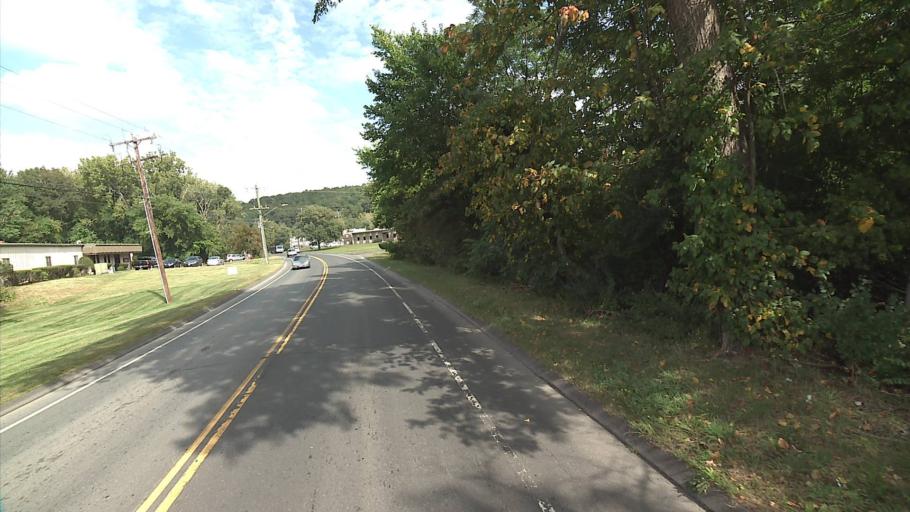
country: US
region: Connecticut
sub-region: Hartford County
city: Newington
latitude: 41.7184
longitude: -72.7159
